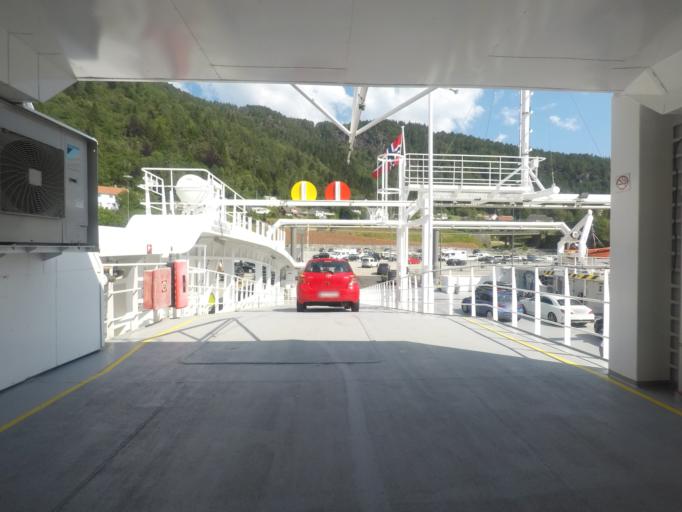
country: NO
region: Sogn og Fjordane
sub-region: Hyllestad
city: Hyllestad
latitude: 61.1043
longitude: 5.5065
